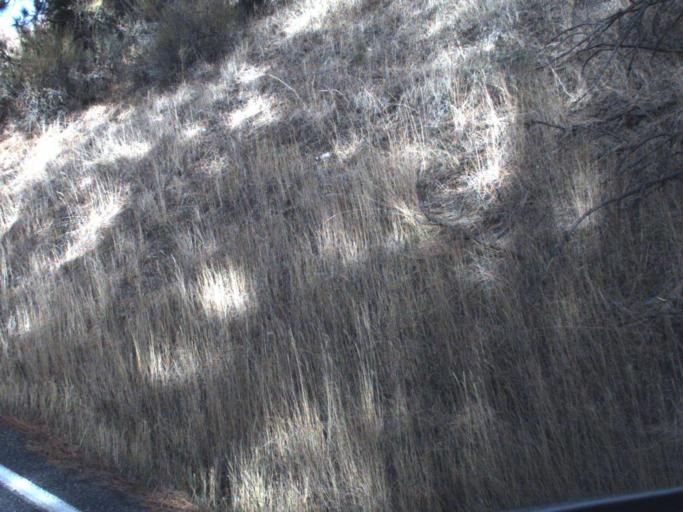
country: US
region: Washington
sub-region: Stevens County
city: Kettle Falls
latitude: 48.3178
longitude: -118.1492
